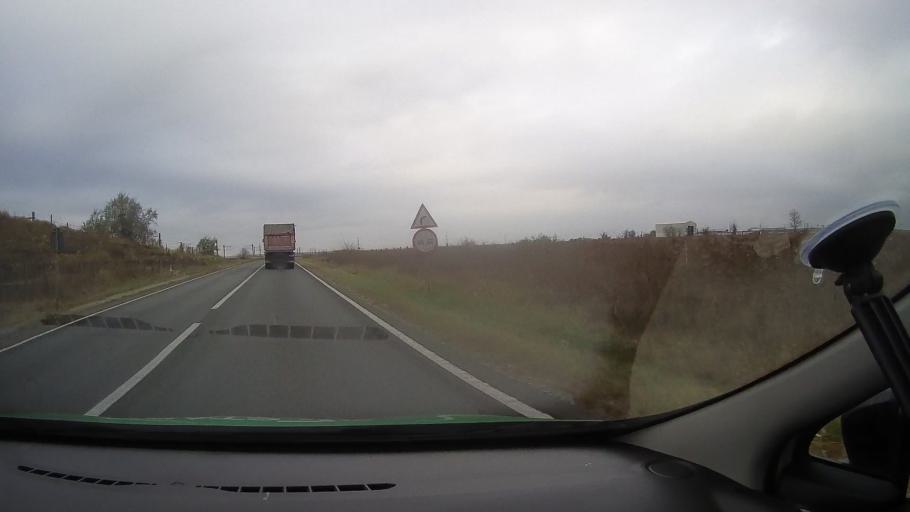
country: RO
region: Constanta
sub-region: Comuna Poarta Alba
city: Poarta Alba
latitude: 44.2288
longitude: 28.3798
